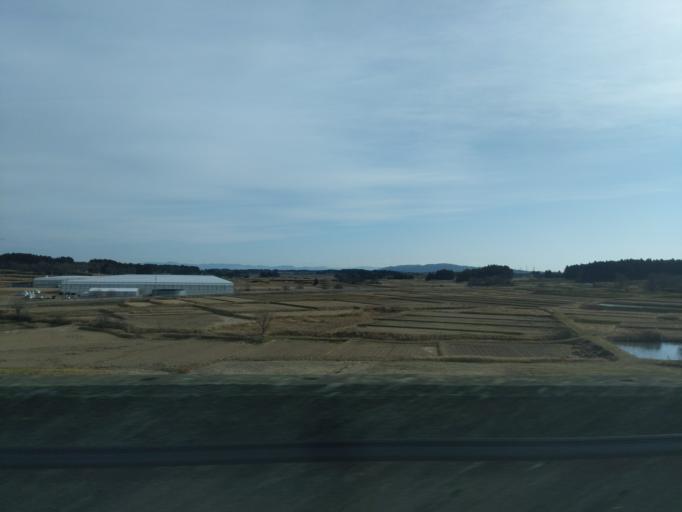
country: JP
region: Miyagi
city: Furukawa
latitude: 38.6451
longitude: 141.0129
